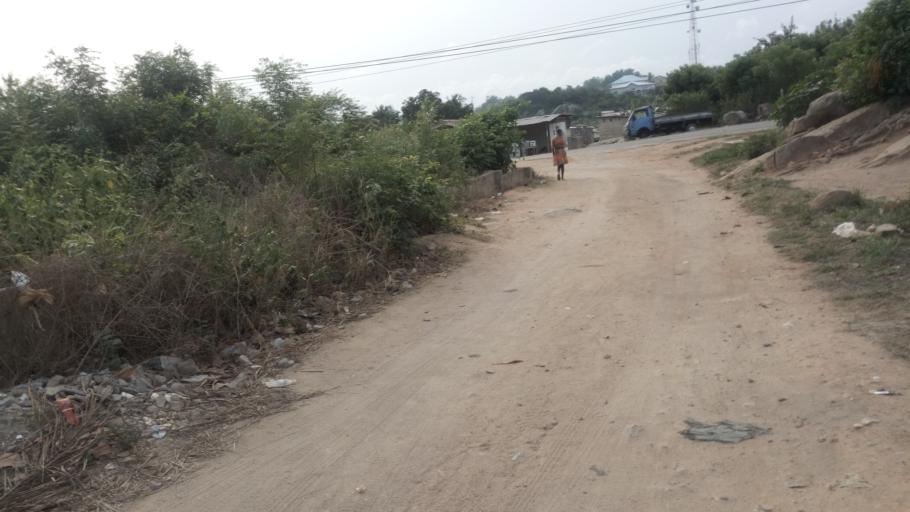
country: GH
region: Central
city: Winneba
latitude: 5.3569
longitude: -0.6240
